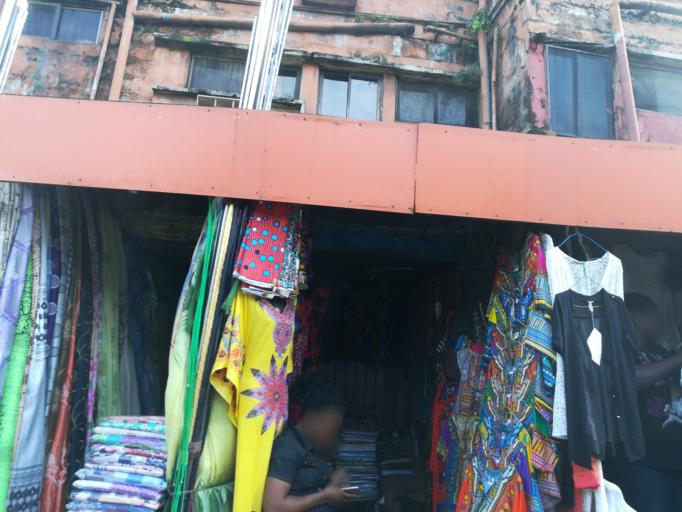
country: NG
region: Lagos
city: Ikeja
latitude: 6.5963
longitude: 3.3431
